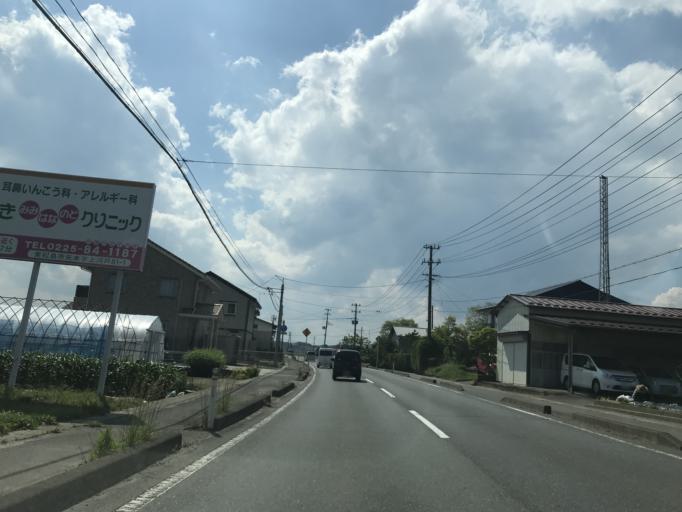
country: JP
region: Miyagi
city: Wakuya
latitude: 38.4737
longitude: 141.1217
